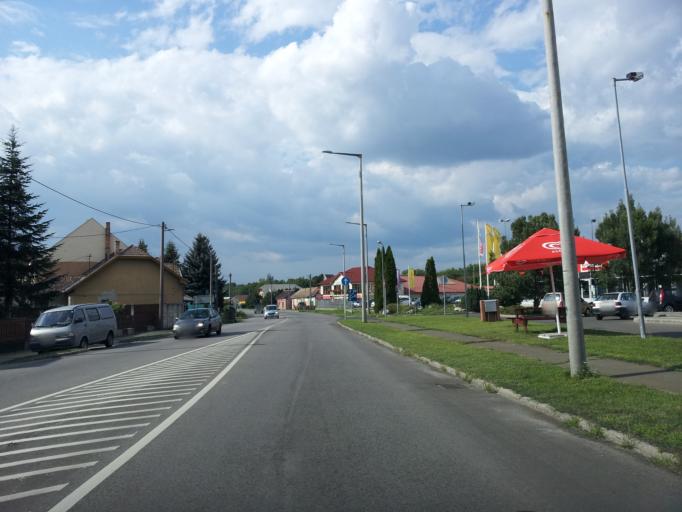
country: HU
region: Pest
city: Vac
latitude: 47.7919
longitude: 19.1162
